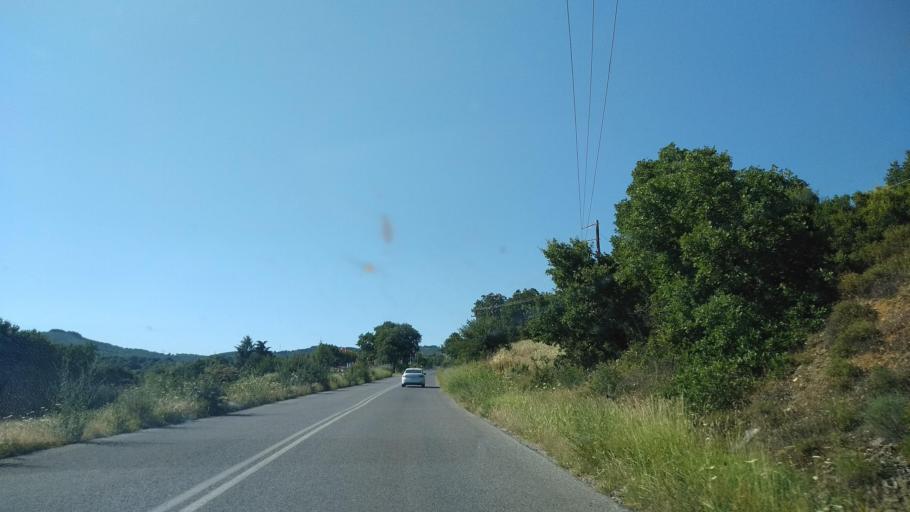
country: GR
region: Central Macedonia
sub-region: Nomos Chalkidikis
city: Megali Panagia
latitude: 40.4336
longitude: 23.6769
